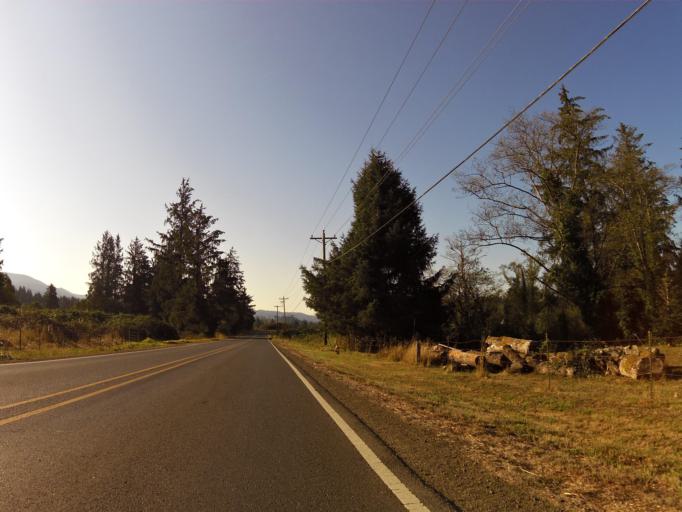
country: US
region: Oregon
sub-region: Tillamook County
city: Tillamook
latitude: 45.4299
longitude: -123.7779
